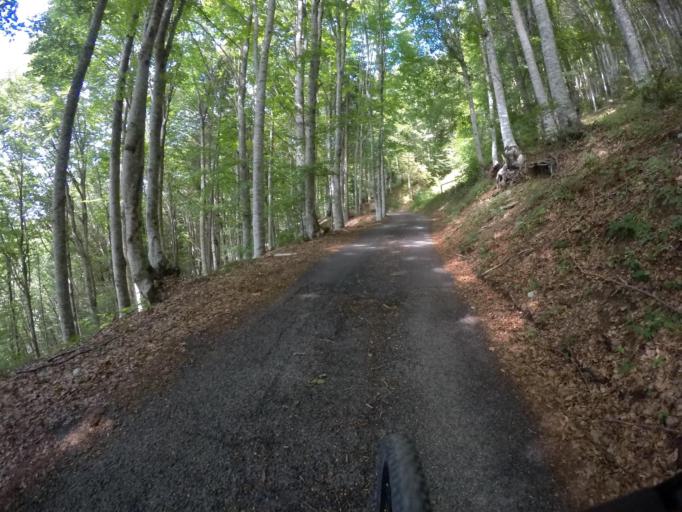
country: IT
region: Friuli Venezia Giulia
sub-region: Provincia di Udine
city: Treppo Carnico
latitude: 46.4957
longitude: 13.0656
